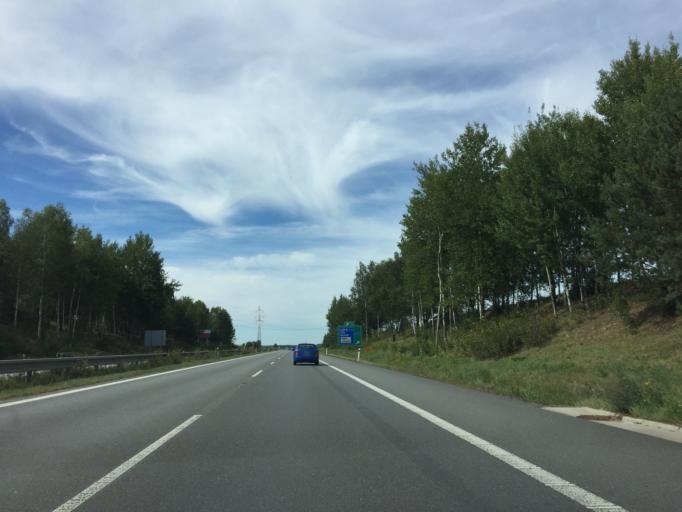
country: CZ
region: Jihocesky
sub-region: Okres Tabor
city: Sezimovo Usti
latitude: 49.4232
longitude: 14.7027
